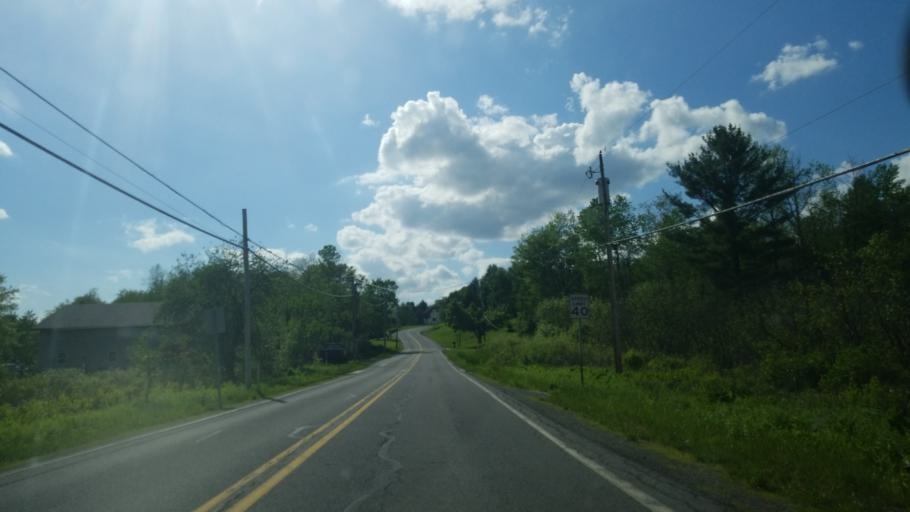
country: US
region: Pennsylvania
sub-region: Clearfield County
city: Troy
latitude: 40.9148
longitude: -78.2575
